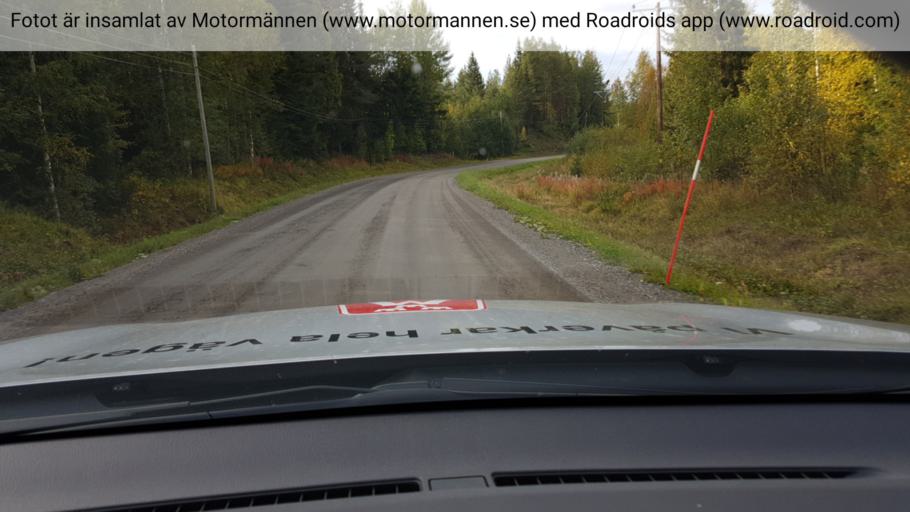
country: SE
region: Jaemtland
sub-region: Stroemsunds Kommun
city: Stroemsund
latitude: 63.9684
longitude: 15.8310
